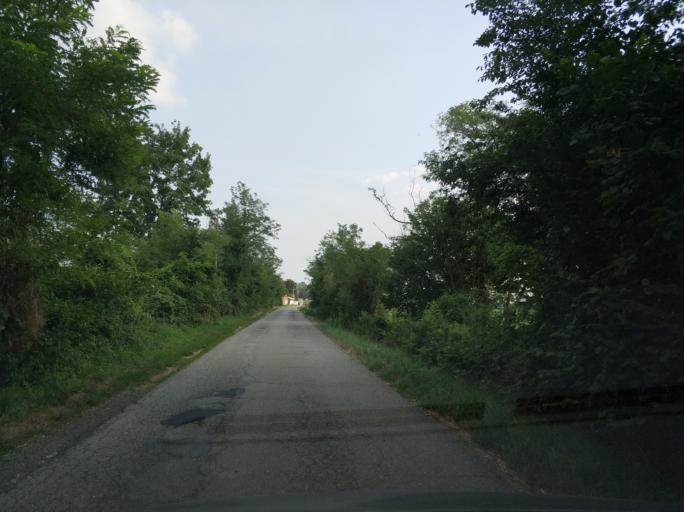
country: IT
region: Piedmont
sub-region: Provincia di Torino
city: Leini
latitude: 45.1865
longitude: 7.6871
